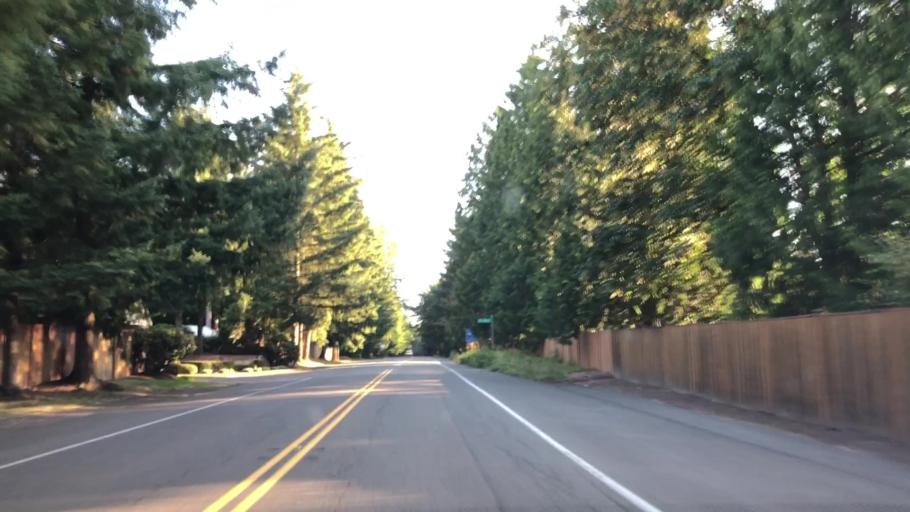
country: US
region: Washington
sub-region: King County
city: Redmond
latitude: 47.7160
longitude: -122.1105
